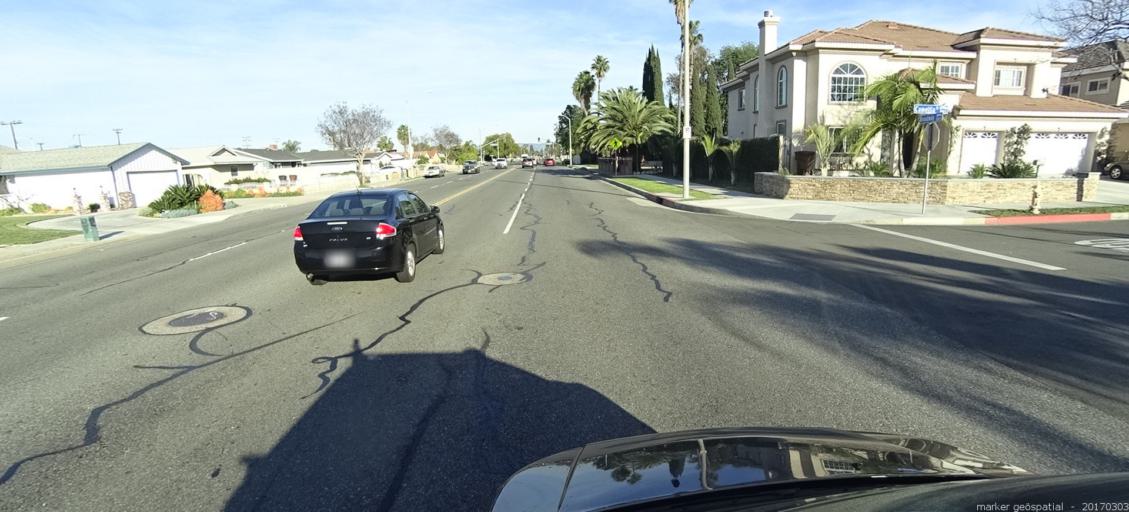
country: US
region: California
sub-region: Orange County
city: Anaheim
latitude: 33.8288
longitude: -117.9537
